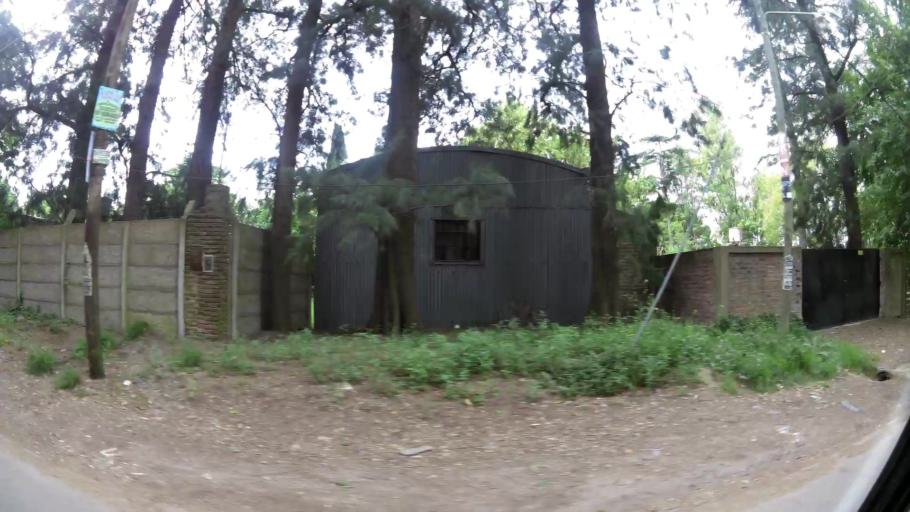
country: AR
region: Buenos Aires
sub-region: Partido de Ezeiza
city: Ezeiza
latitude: -34.8722
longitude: -58.5035
